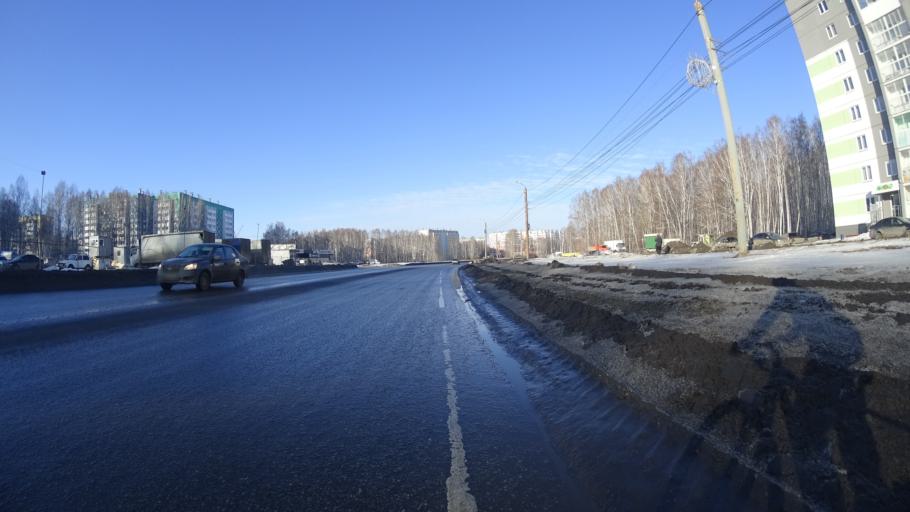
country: RU
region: Chelyabinsk
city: Roshchino
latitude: 55.2122
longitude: 61.2843
